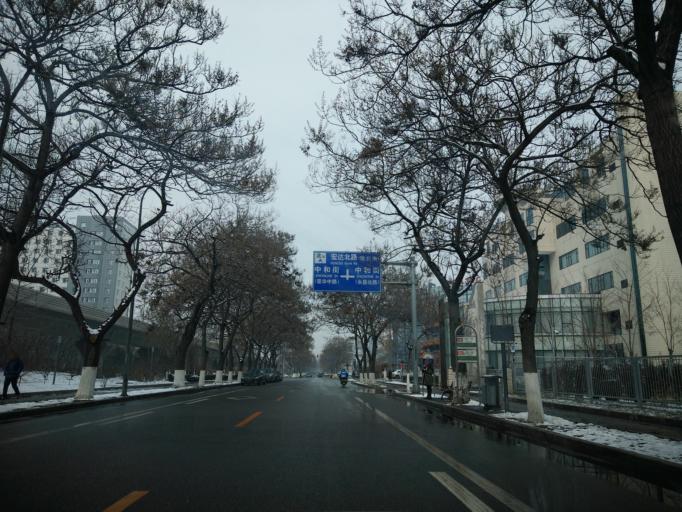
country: CN
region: Beijing
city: Jiugong
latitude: 39.7952
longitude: 116.5052
